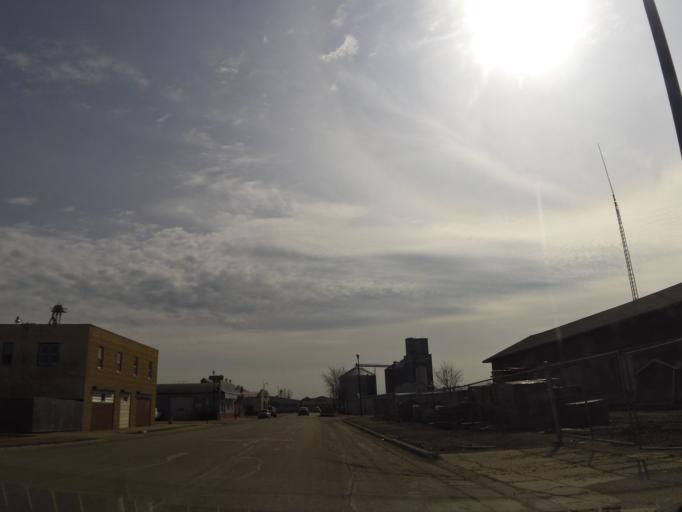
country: US
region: North Dakota
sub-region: Walsh County
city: Grafton
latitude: 48.4212
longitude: -97.4087
